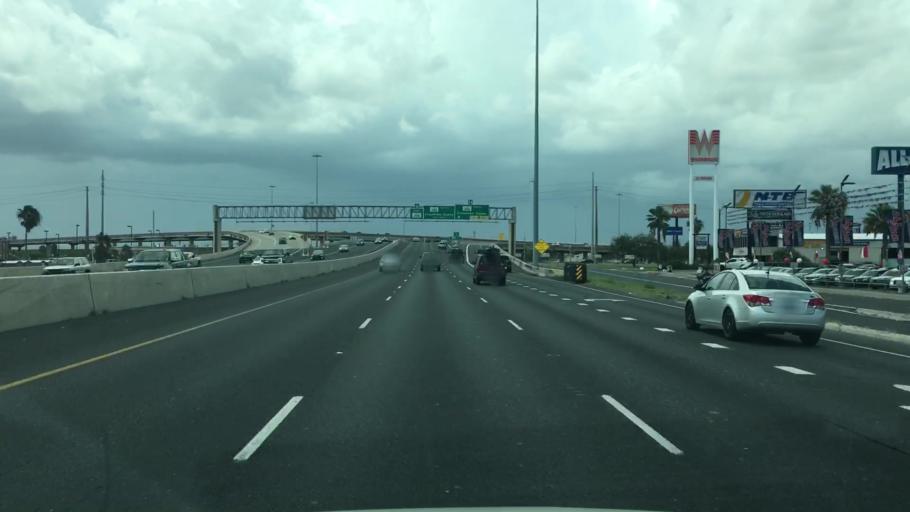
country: US
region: Texas
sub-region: Nueces County
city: Corpus Christi
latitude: 27.7344
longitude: -97.4248
